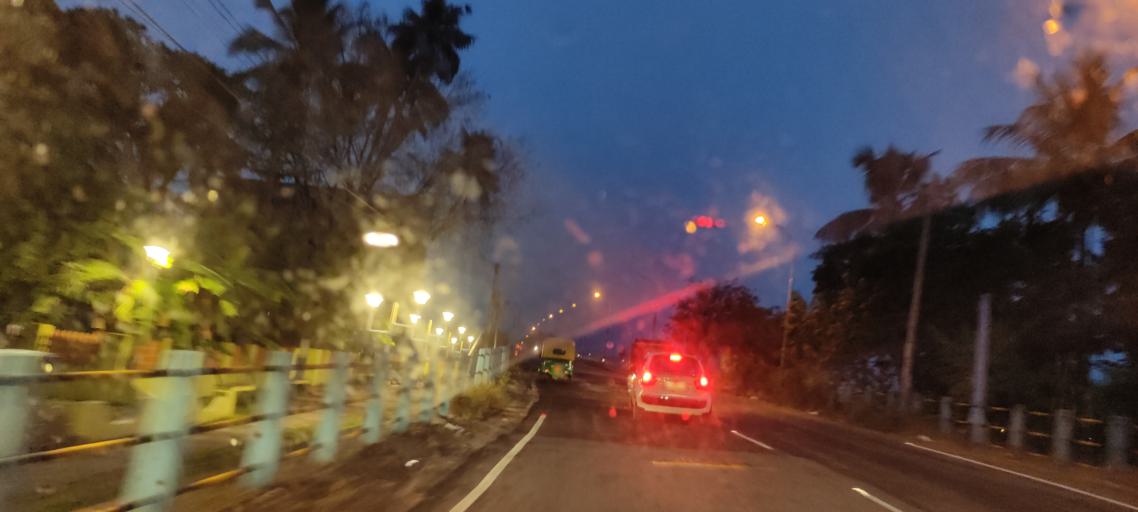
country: IN
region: Kerala
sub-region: Ernakulam
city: Cochin
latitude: 9.8938
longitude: 76.2959
